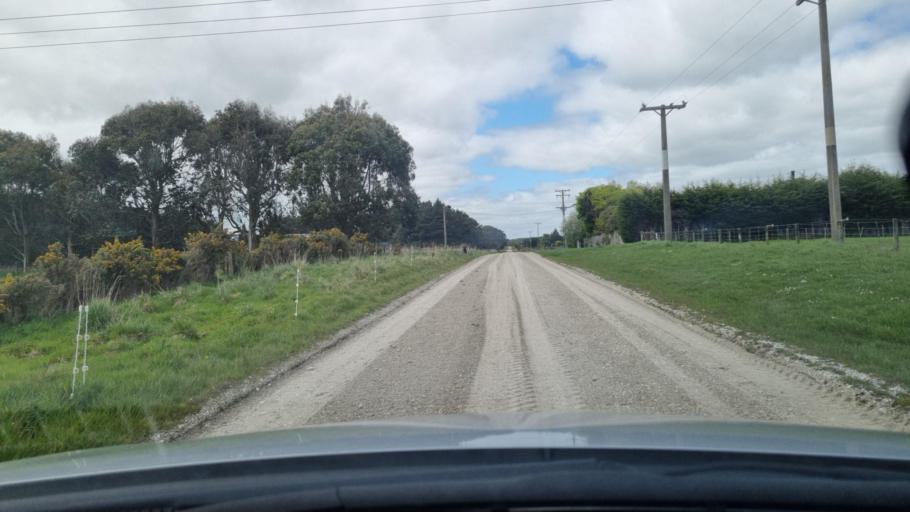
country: NZ
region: Southland
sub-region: Invercargill City
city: Invercargill
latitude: -46.4343
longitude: 168.4013
